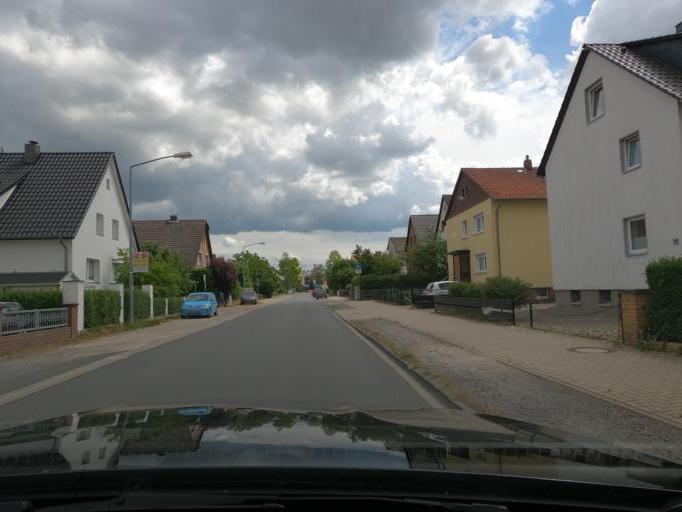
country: DE
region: Lower Saxony
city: Sehnde
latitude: 52.3097
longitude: 9.9691
